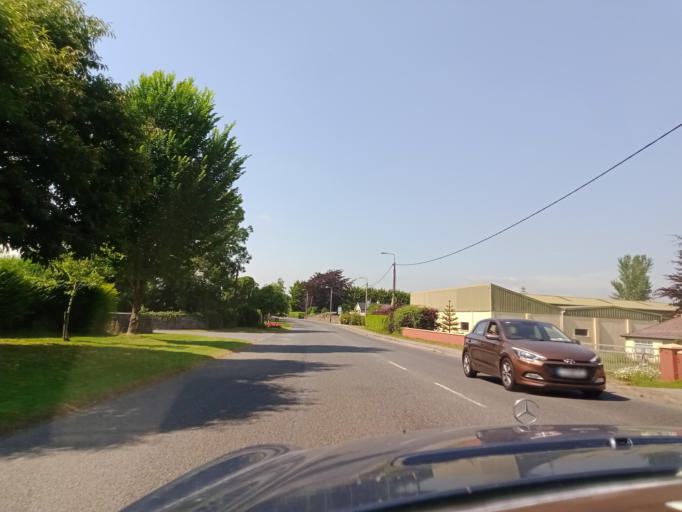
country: IE
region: Leinster
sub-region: Kilkenny
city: Piltown
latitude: 52.3439
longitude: -7.3199
